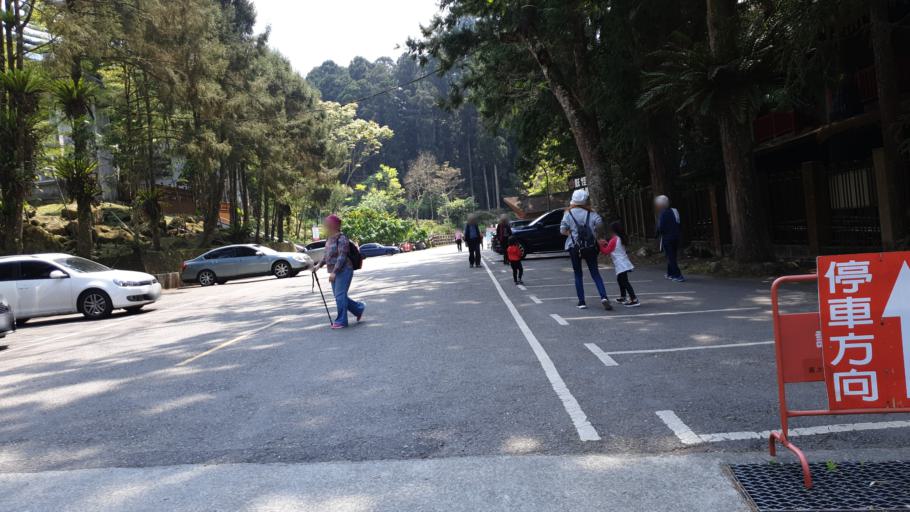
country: TW
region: Taiwan
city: Lugu
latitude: 23.6743
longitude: 120.7979
